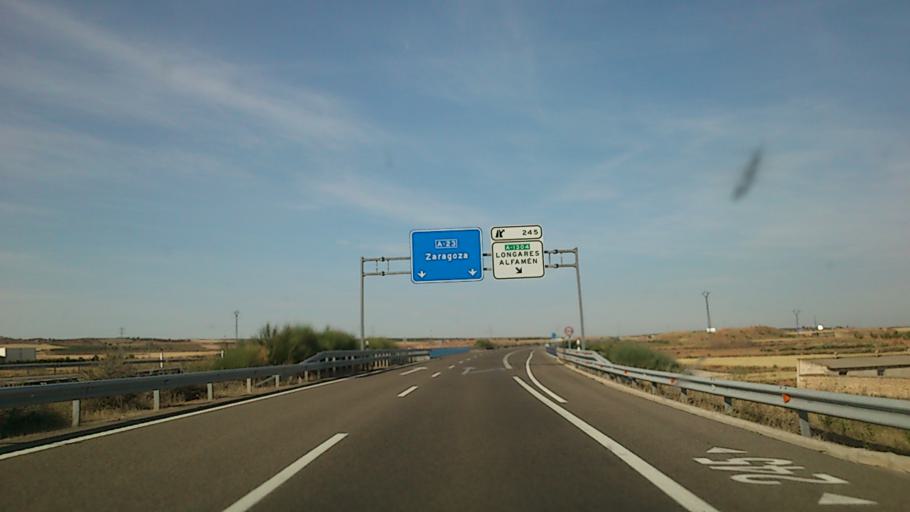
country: ES
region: Aragon
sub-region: Provincia de Zaragoza
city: Longares
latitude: 41.4038
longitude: -1.1782
